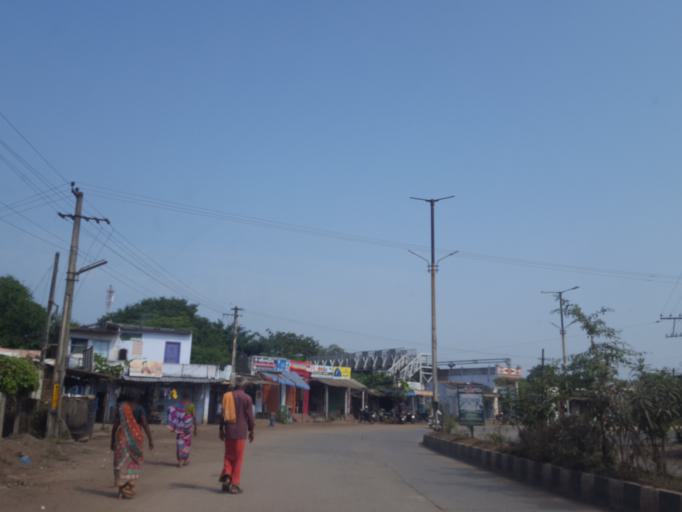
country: IN
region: Telangana
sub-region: Khammam
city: Yellandu
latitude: 17.5925
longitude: 80.3196
